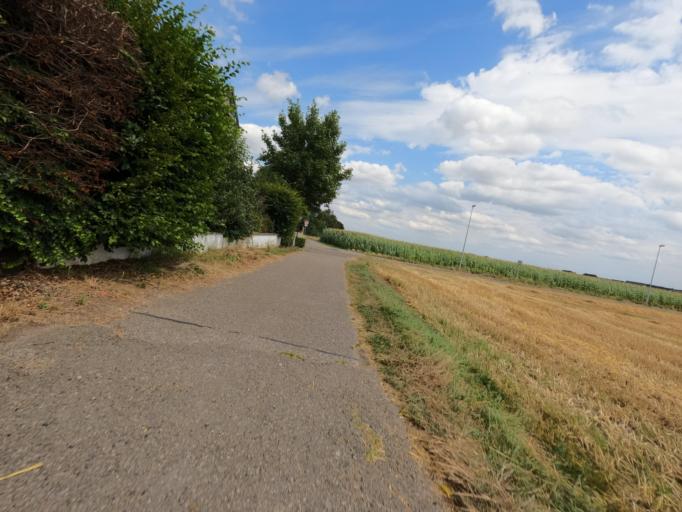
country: DE
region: North Rhine-Westphalia
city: Geilenkirchen
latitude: 50.9780
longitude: 6.1087
